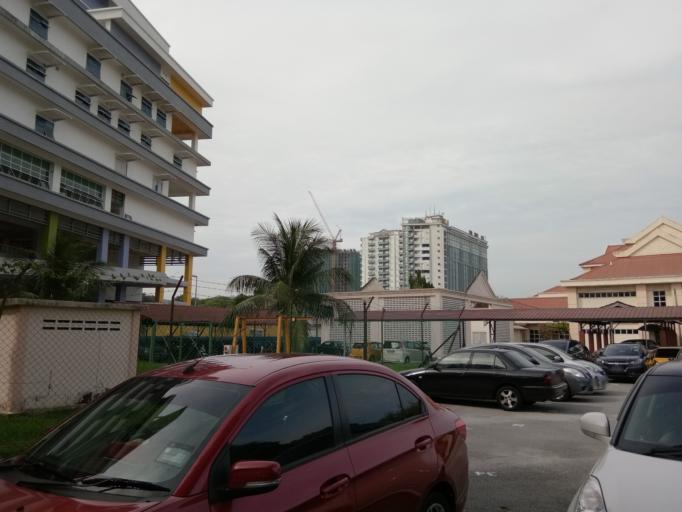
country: MY
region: Perak
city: Ipoh
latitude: 4.6037
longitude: 101.0875
